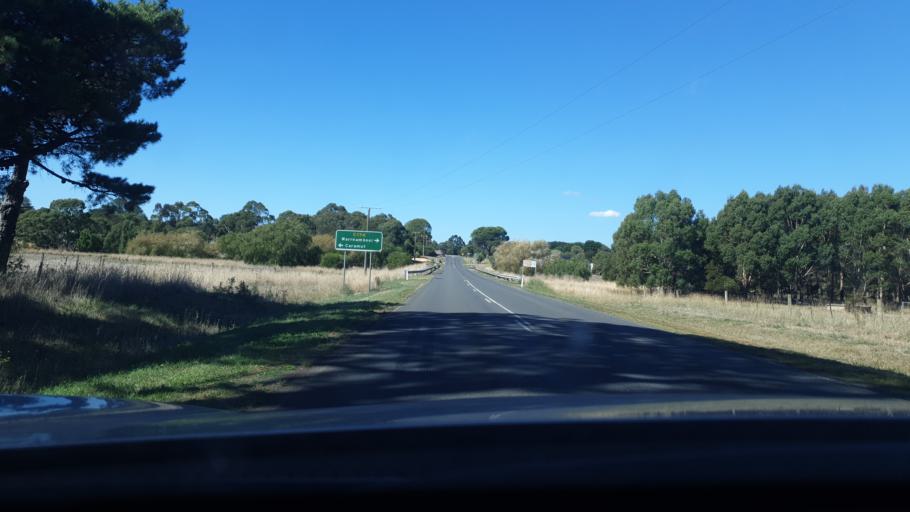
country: AU
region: Victoria
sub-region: Warrnambool
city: Warrnambool
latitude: -38.1842
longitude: 142.4277
